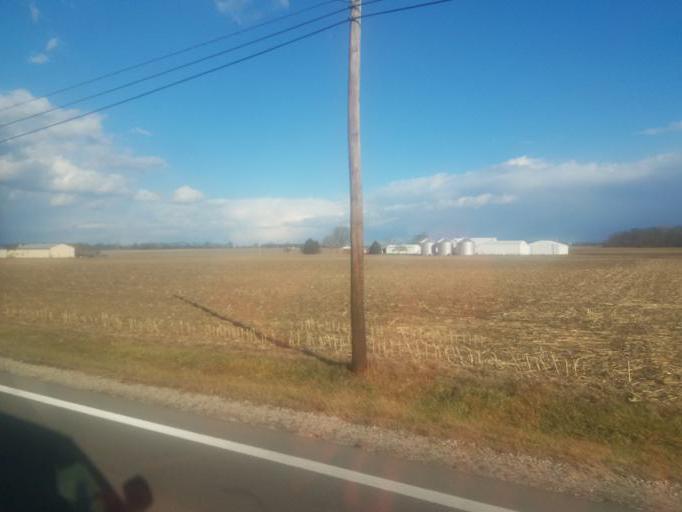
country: US
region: Ohio
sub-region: Marion County
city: Prospect
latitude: 40.3656
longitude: -83.1474
